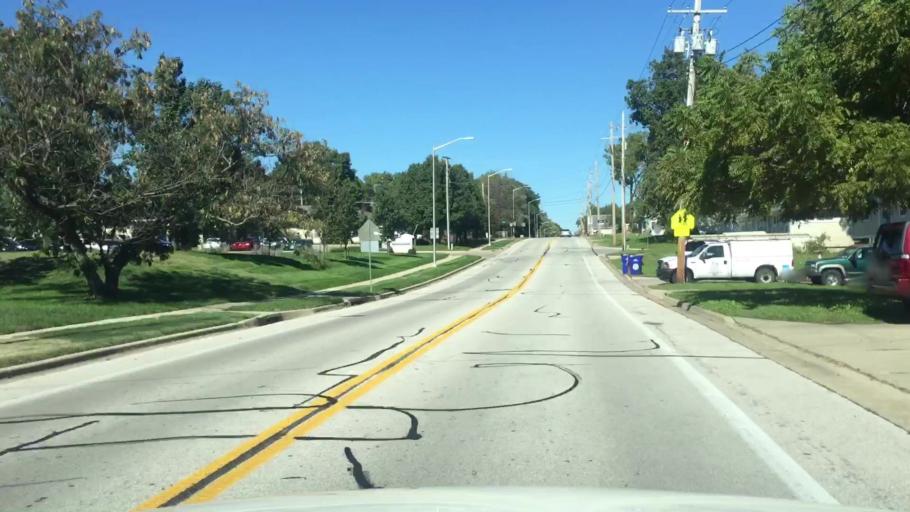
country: US
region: Kansas
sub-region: Johnson County
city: Shawnee
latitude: 39.0225
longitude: -94.7332
